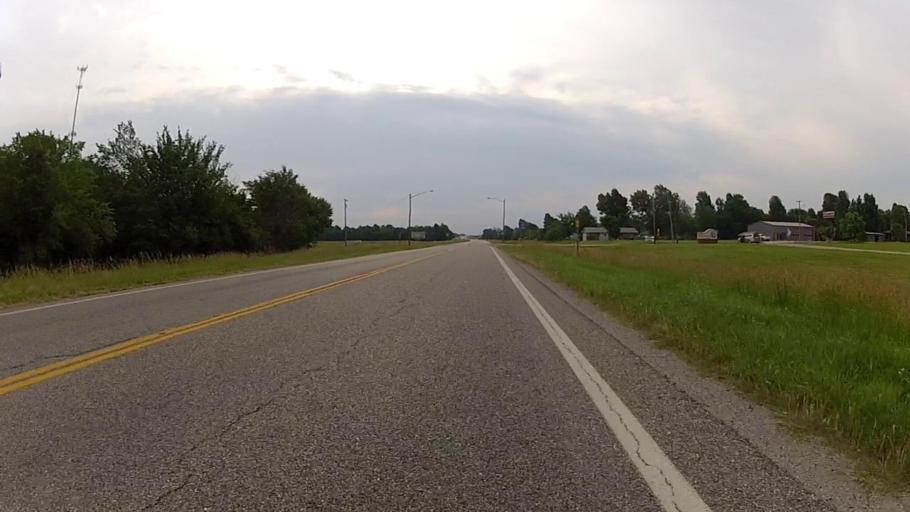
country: US
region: Kansas
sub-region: Cherokee County
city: Columbus
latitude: 37.1786
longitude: -94.8507
